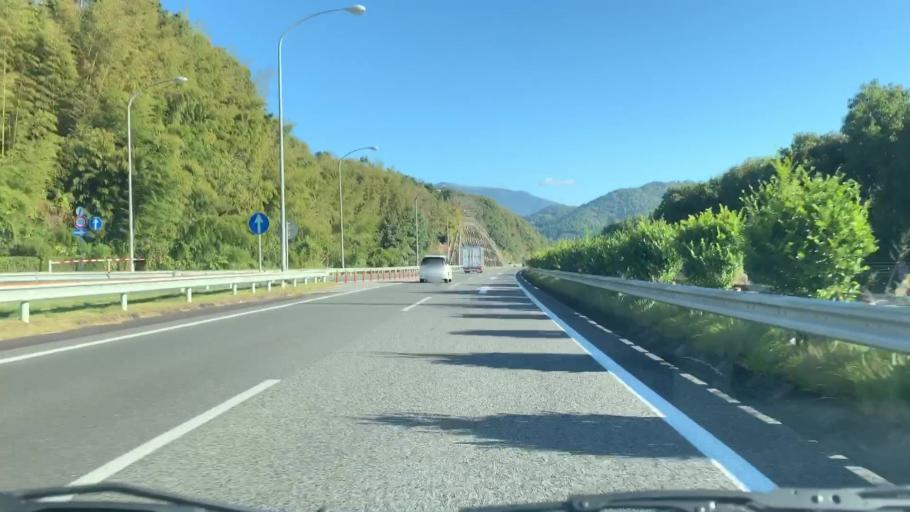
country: JP
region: Saga Prefecture
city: Takeocho-takeo
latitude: 33.2627
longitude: 130.0837
